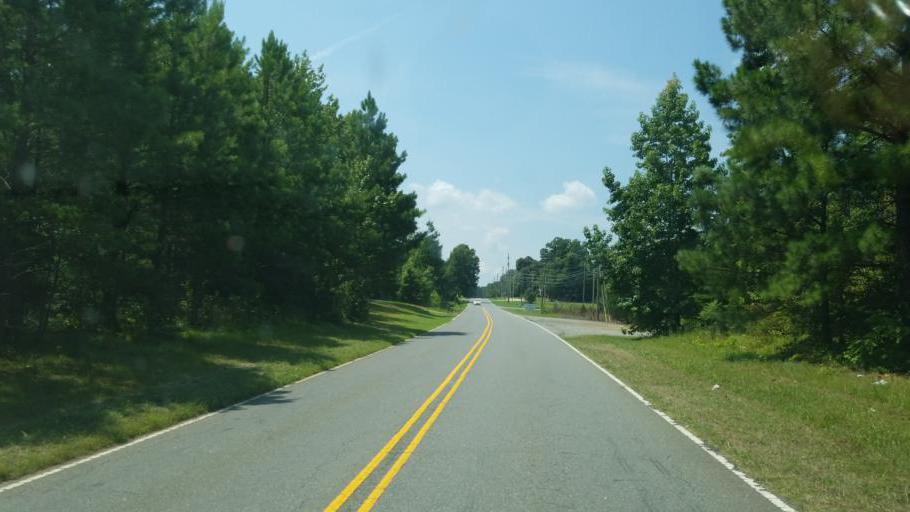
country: US
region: North Carolina
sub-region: Gaston County
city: Tryon
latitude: 35.3225
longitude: -81.3643
